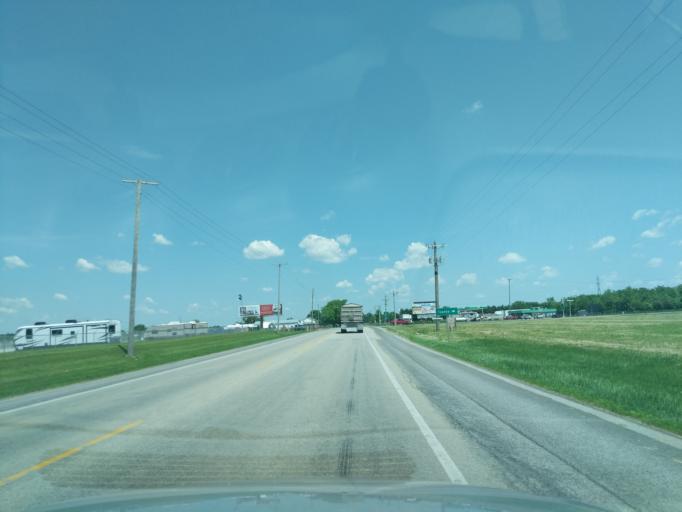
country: US
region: Indiana
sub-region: LaGrange County
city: Topeka
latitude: 41.5375
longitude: -85.5779
